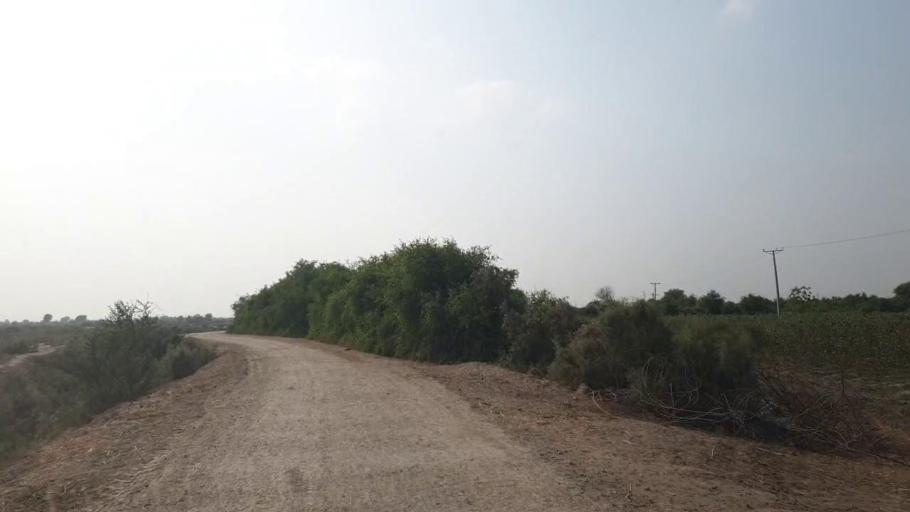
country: PK
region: Sindh
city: Rajo Khanani
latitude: 25.0236
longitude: 68.7968
